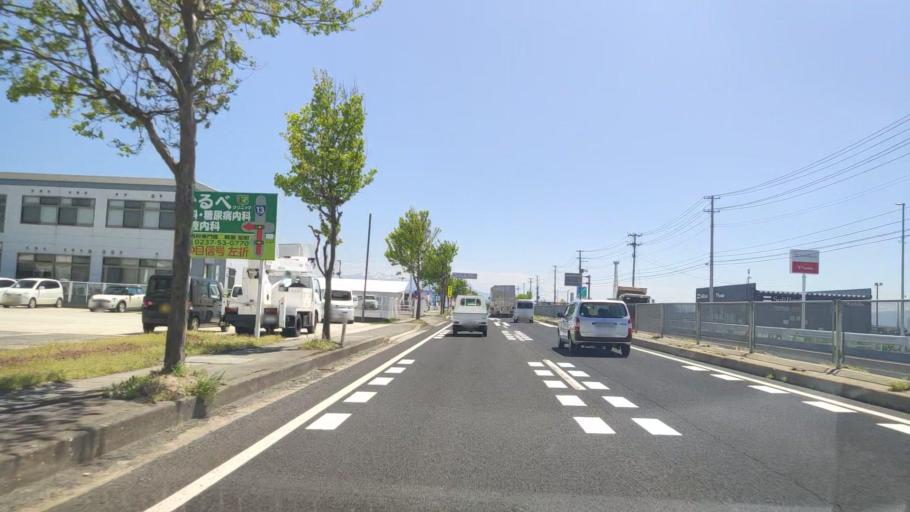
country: JP
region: Yamagata
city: Higashine
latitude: 38.4792
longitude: 140.3829
